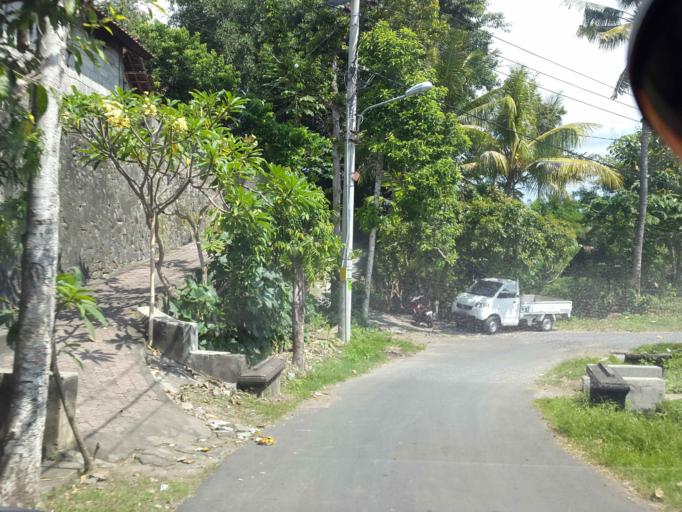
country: ID
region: Bali
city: Klungkung
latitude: -8.5619
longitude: 115.3815
